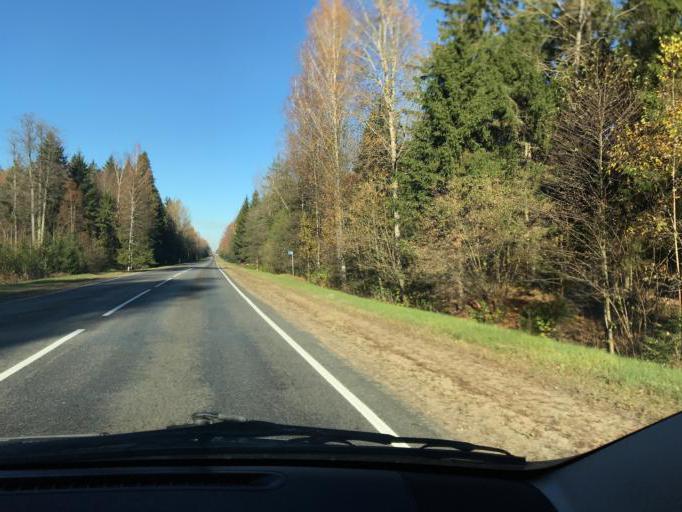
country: BY
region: Vitebsk
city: Polatsk
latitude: 55.4194
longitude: 28.7918
